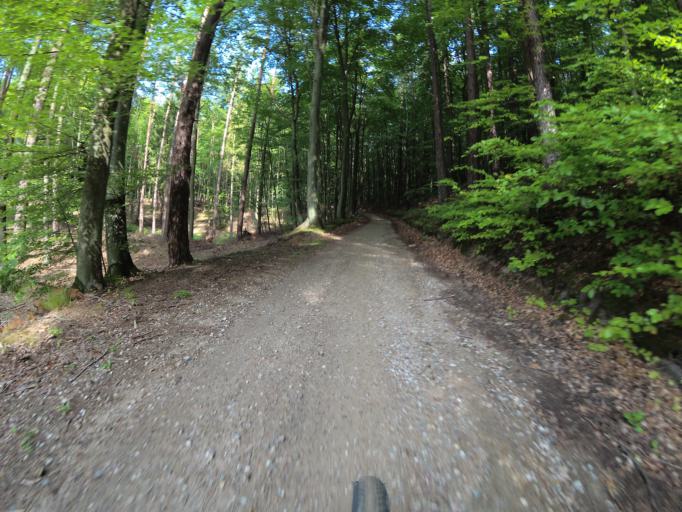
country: PL
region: Pomeranian Voivodeship
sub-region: Gdynia
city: Wielki Kack
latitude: 54.4936
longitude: 18.4767
